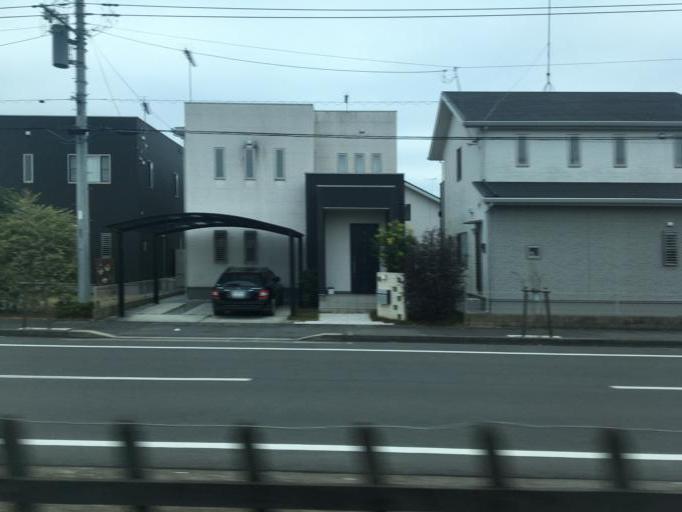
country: JP
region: Tochigi
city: Oyama
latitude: 36.3051
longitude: 139.8216
